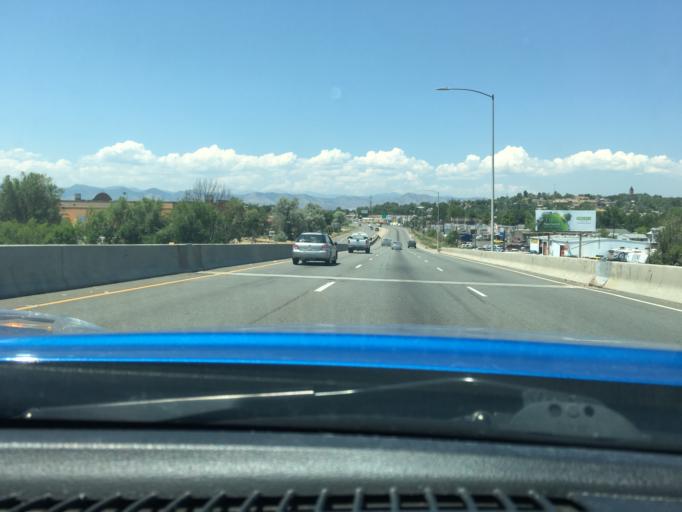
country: US
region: Colorado
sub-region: Arapahoe County
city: Englewood
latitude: 39.6536
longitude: -105.0055
